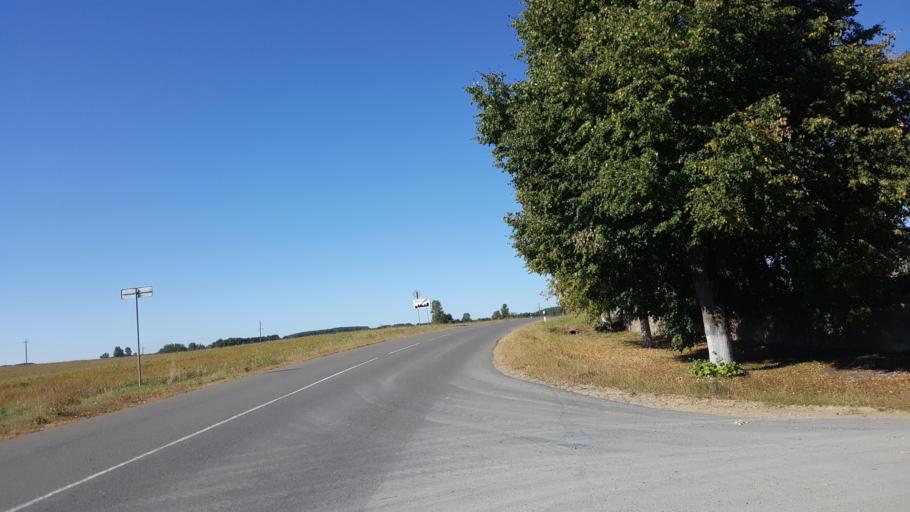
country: BY
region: Brest
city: Kamyanyets
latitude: 52.3920
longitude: 23.7604
